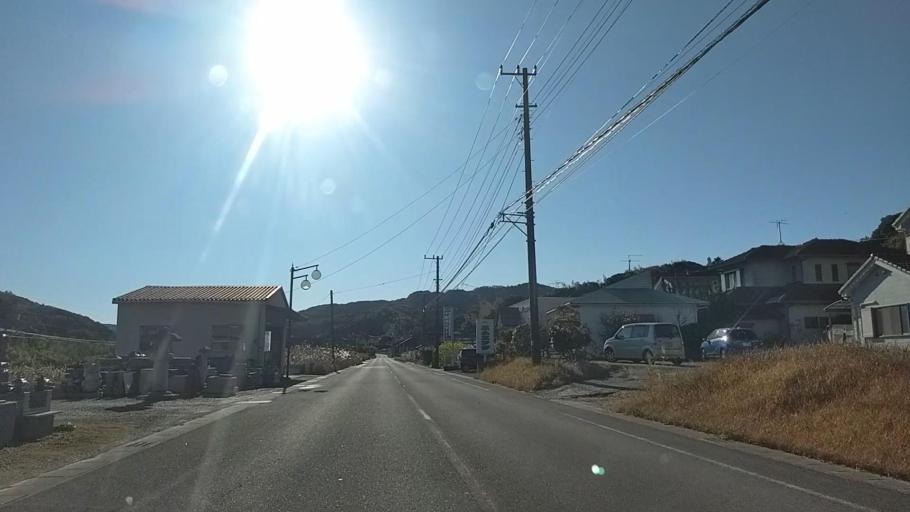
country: JP
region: Chiba
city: Futtsu
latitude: 35.2747
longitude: 139.8622
